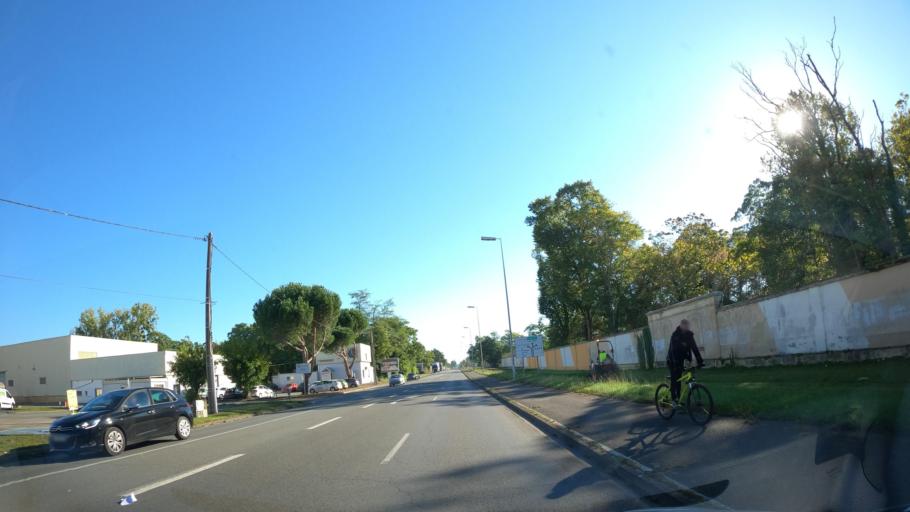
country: FR
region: Aquitaine
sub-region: Departement de la Dordogne
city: Bergerac
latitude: 44.8446
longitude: 0.5070
